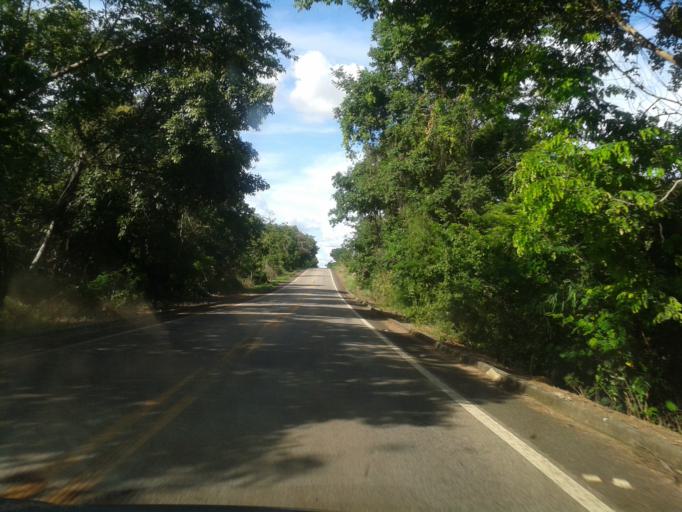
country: BR
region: Goias
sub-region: Mozarlandia
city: Mozarlandia
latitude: -14.6847
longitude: -50.5402
